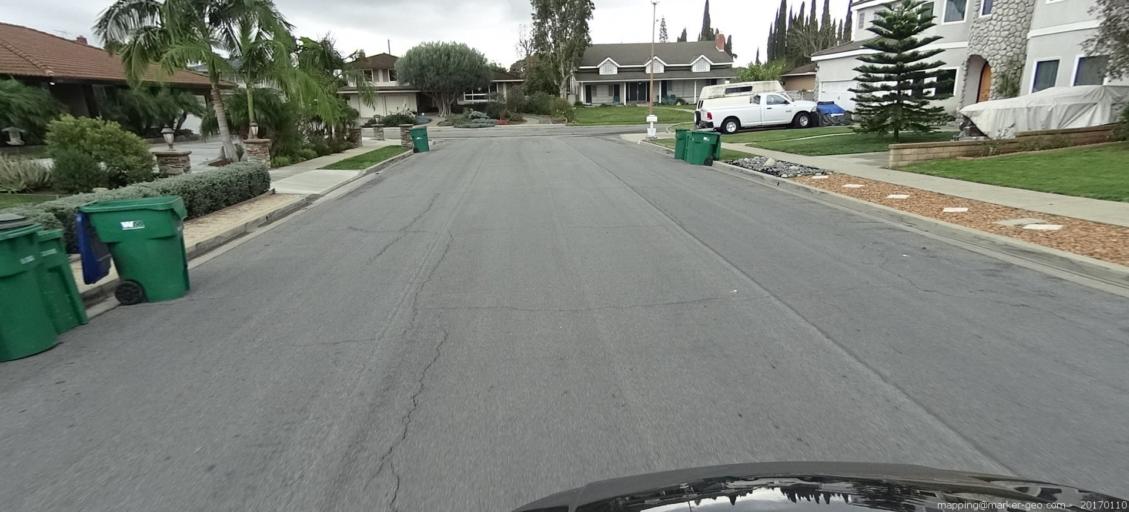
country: US
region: California
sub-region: Orange County
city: Tustin
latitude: 33.7718
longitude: -117.8230
